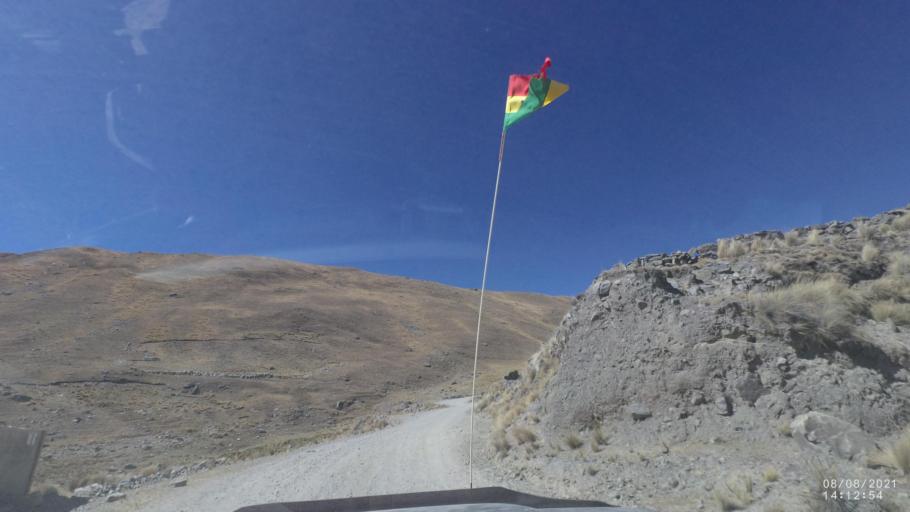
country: BO
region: Cochabamba
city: Sipe Sipe
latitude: -17.1653
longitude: -66.4258
